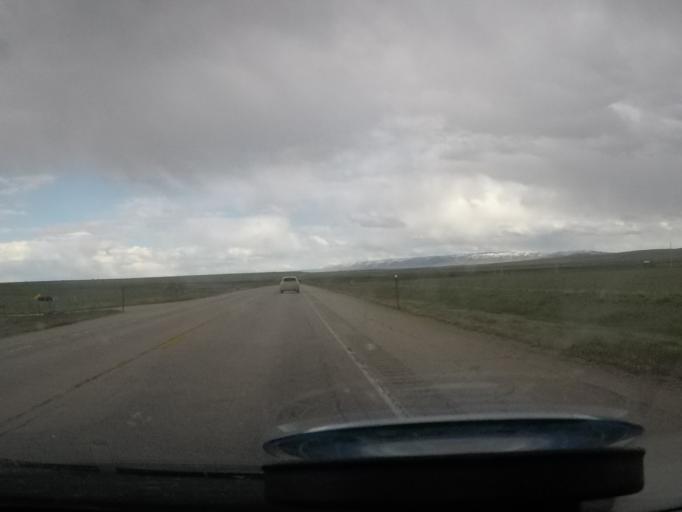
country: US
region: Wyoming
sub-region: Natrona County
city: Mills
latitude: 42.9546
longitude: -106.6447
